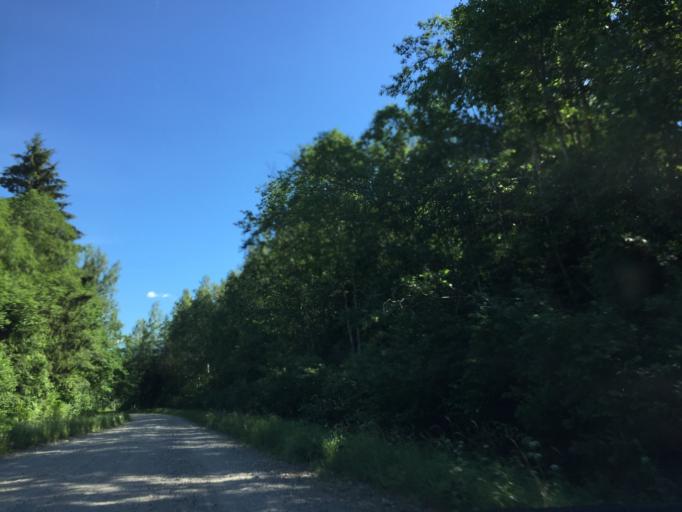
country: LV
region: Dundaga
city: Dundaga
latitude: 57.3363
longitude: 22.0287
